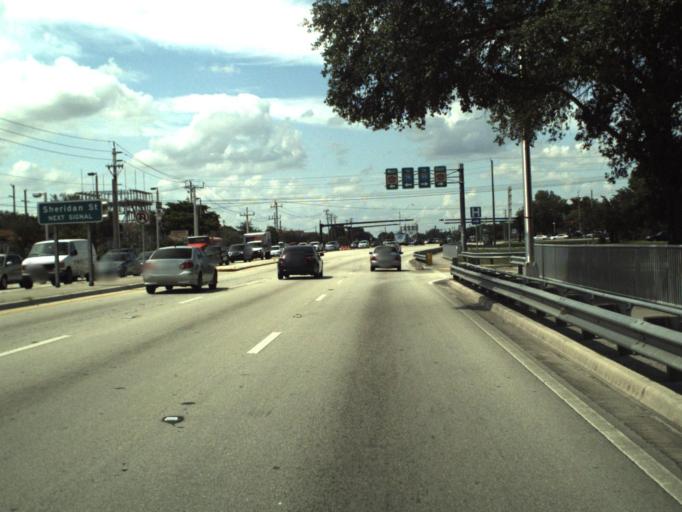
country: US
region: Florida
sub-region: Broward County
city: Pembroke Pines
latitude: 26.0288
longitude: -80.2488
